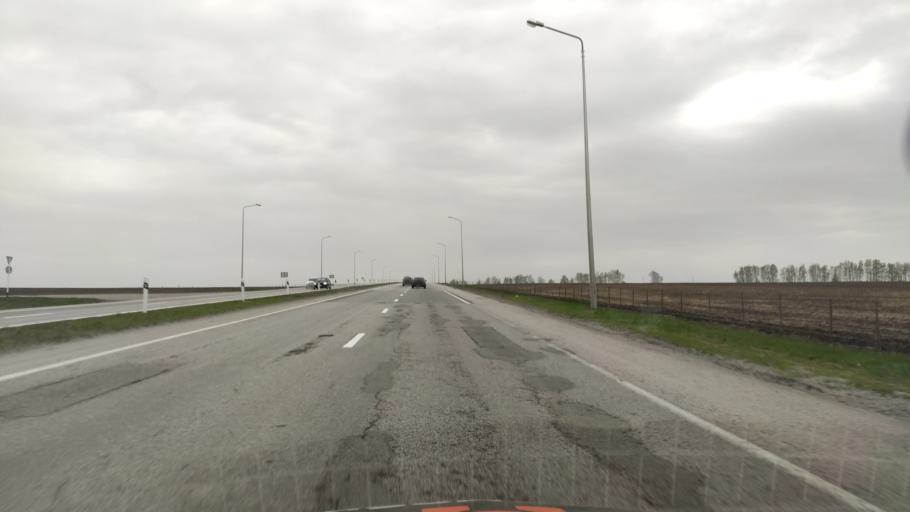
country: RU
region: Belgorod
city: Staryy Oskol
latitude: 51.3355
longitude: 37.7629
